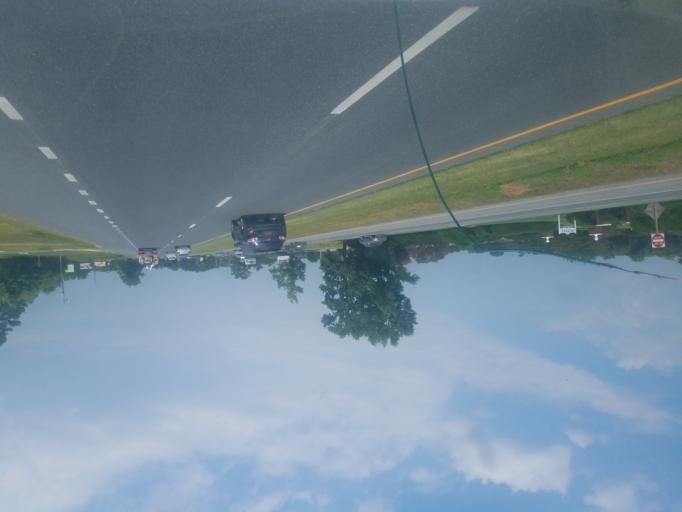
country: US
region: Maryland
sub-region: Worcester County
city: Berlin
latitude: 38.3452
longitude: -75.1834
